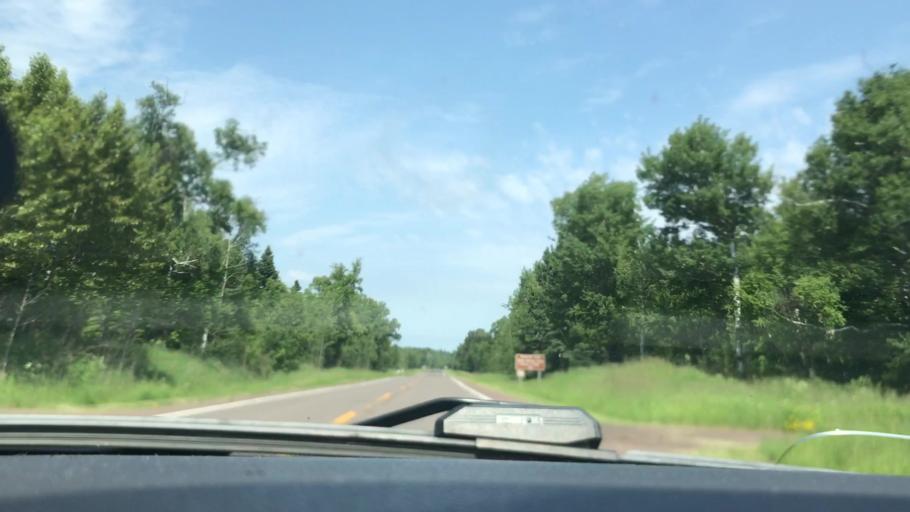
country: US
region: Minnesota
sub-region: Lake County
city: Silver Bay
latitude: 47.4867
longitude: -90.9890
